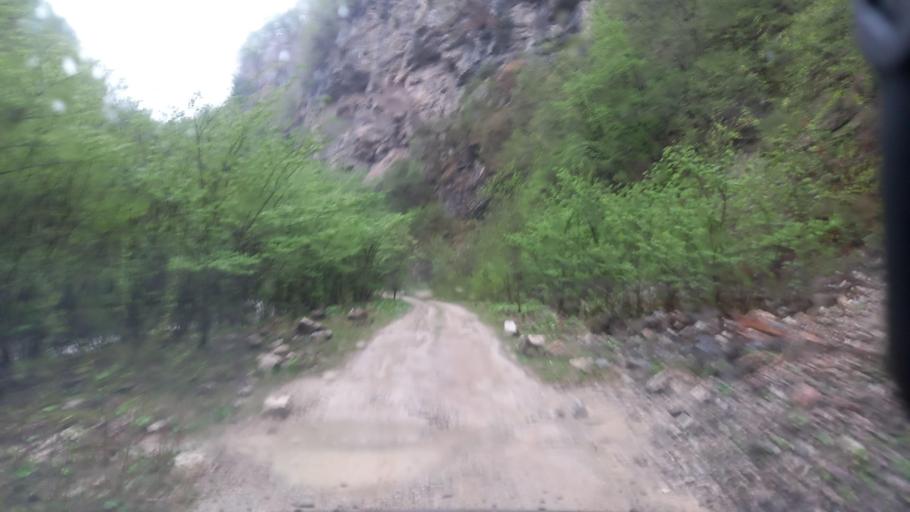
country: RU
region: Kabardino-Balkariya
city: Bylym
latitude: 43.5856
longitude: 43.0099
